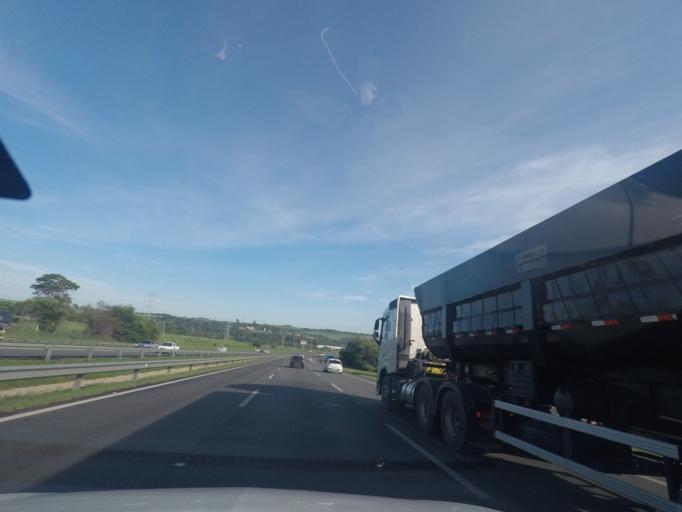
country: BR
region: Sao Paulo
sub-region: Americana
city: Americana
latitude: -22.6977
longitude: -47.3084
